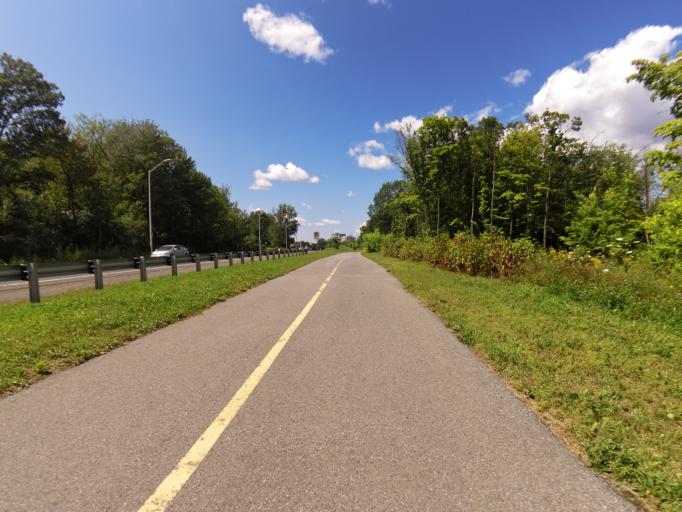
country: CA
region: Ontario
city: Ottawa
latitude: 45.3702
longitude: -75.6722
